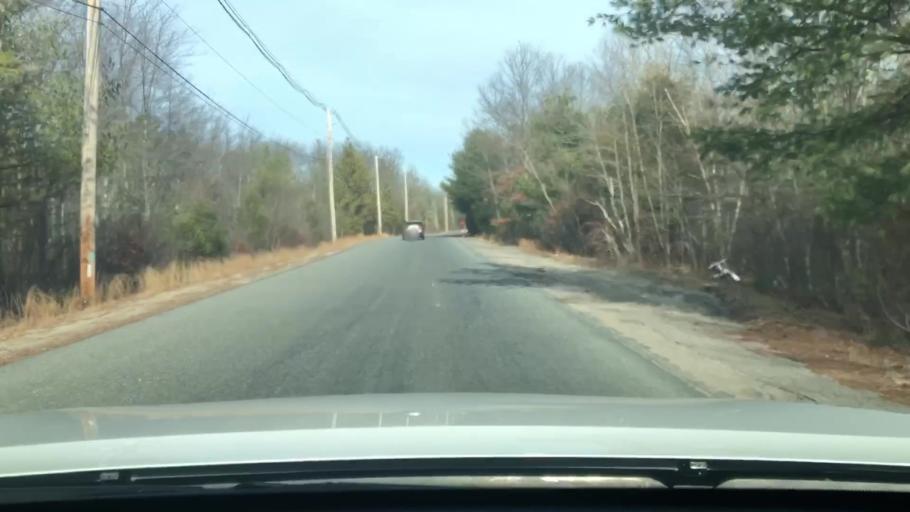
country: US
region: Massachusetts
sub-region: Worcester County
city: Milford
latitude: 42.1432
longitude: -71.4879
